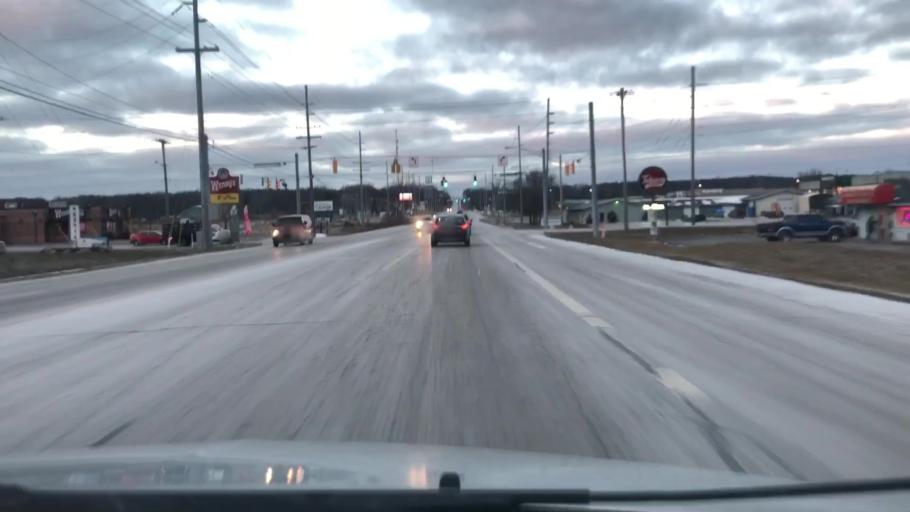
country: US
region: Indiana
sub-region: Steuben County
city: Angola
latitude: 41.6711
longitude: -84.9996
